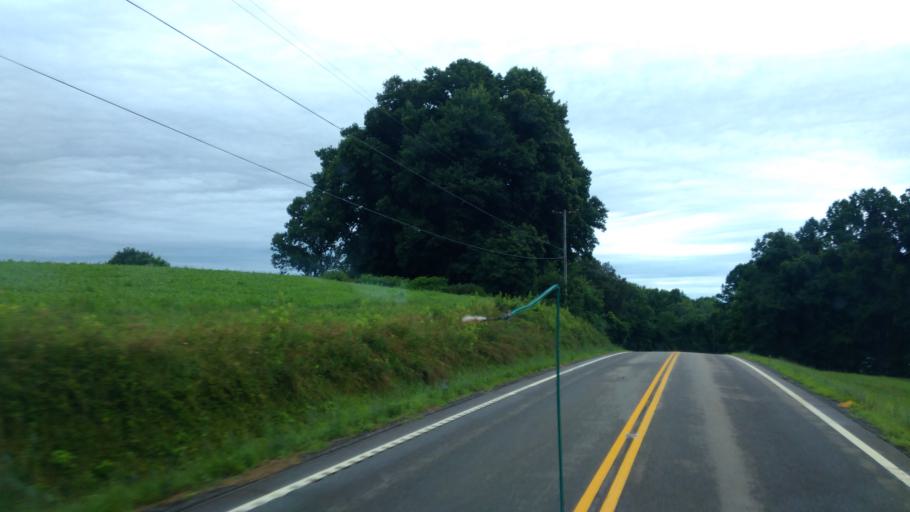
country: US
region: Ohio
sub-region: Stark County
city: Minerva
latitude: 40.6942
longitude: -81.0131
